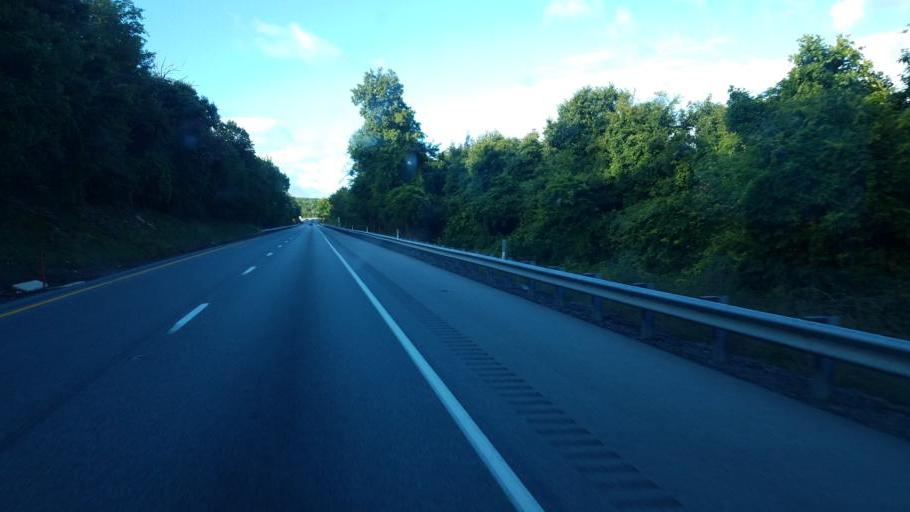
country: US
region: Pennsylvania
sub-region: Bedford County
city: Earlston
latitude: 39.8941
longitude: -78.2424
